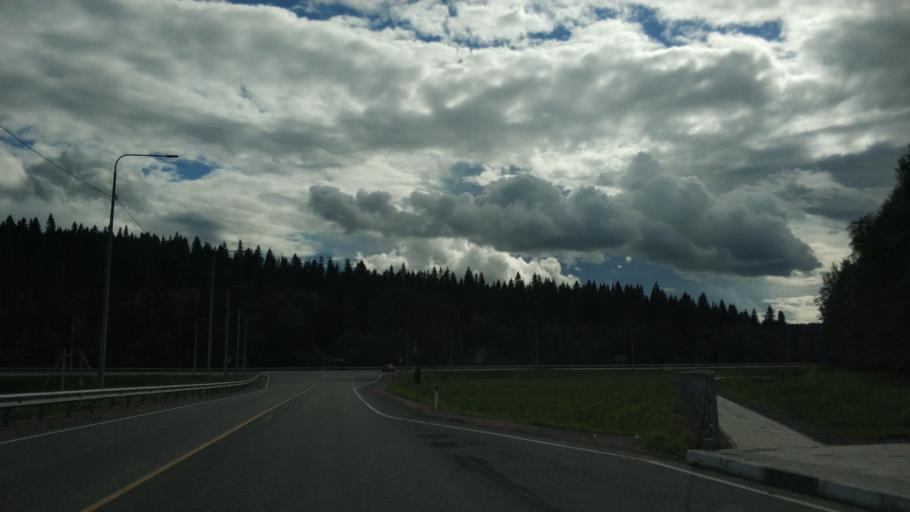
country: RU
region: Republic of Karelia
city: Khelyulya
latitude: 61.7770
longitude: 30.6611
